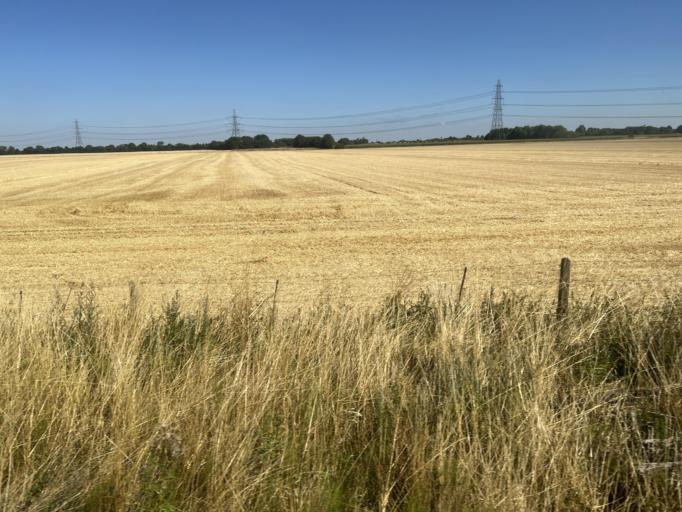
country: GB
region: England
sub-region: Lincolnshire
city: Heckington
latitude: 52.9748
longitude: -0.2801
